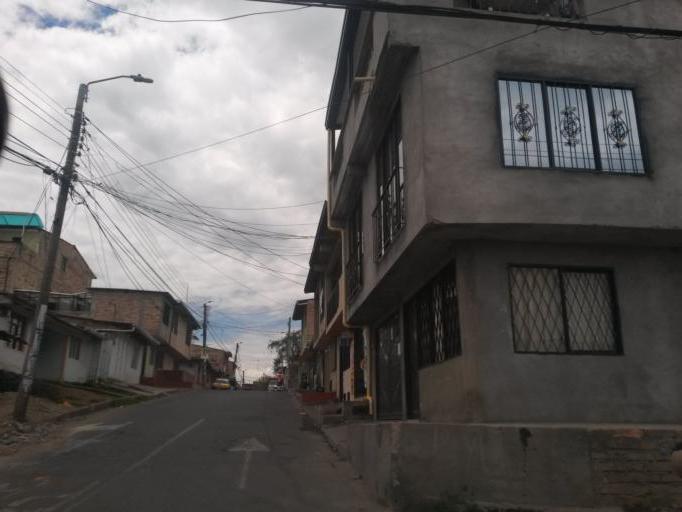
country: CO
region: Cauca
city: Popayan
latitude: 2.4491
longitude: -76.6296
